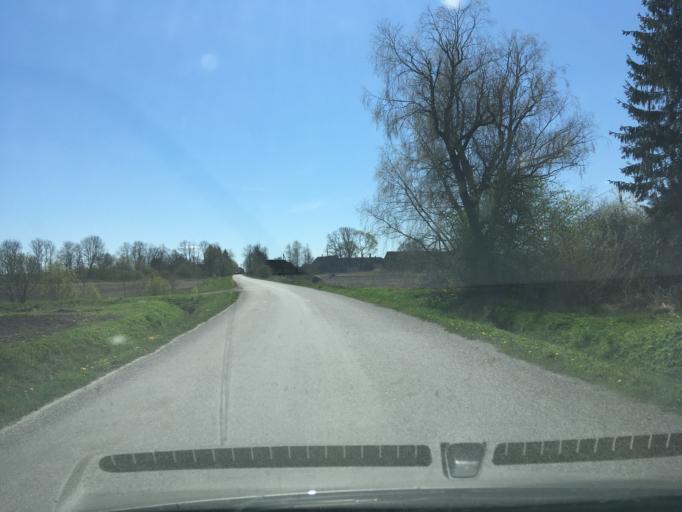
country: EE
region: Harju
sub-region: Raasiku vald
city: Arukula
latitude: 59.3938
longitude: 25.0792
